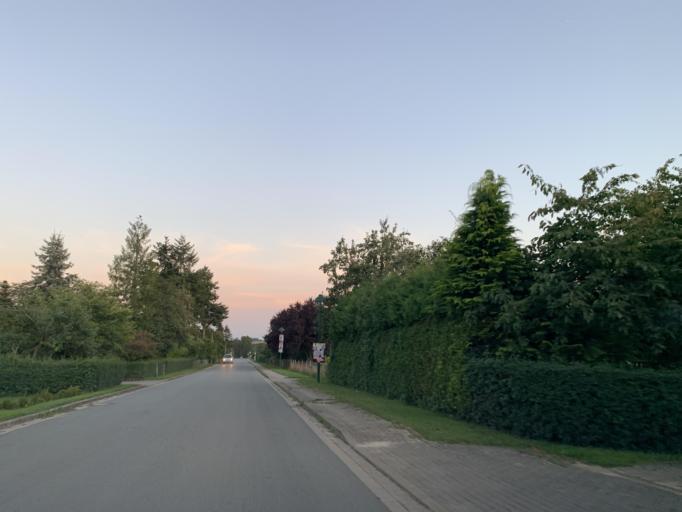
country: DE
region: Mecklenburg-Vorpommern
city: Blankensee
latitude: 53.4441
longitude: 13.2977
